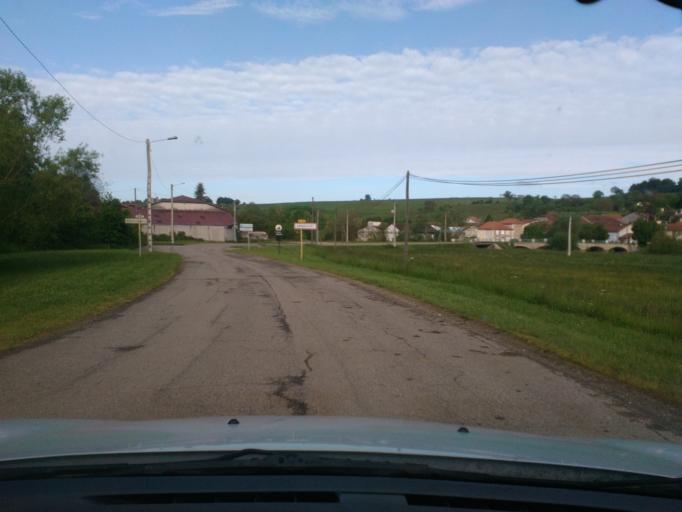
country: FR
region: Lorraine
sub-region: Departement des Vosges
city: Mirecourt
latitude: 48.3461
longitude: 6.1455
